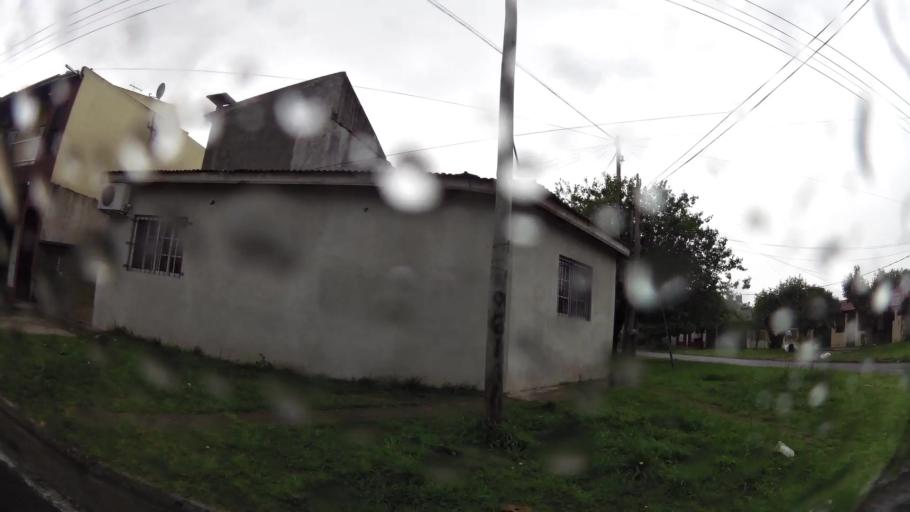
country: AR
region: Buenos Aires
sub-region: Partido de Quilmes
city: Quilmes
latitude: -34.7748
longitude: -58.2265
